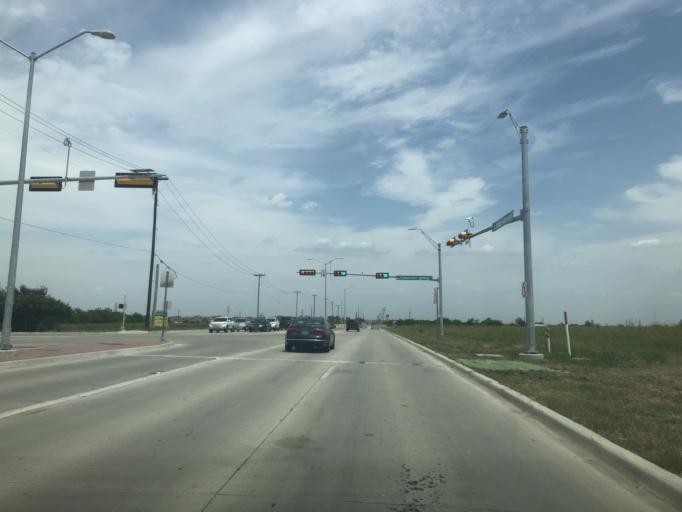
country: US
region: Texas
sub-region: Tarrant County
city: Saginaw
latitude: 32.8837
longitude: -97.3668
